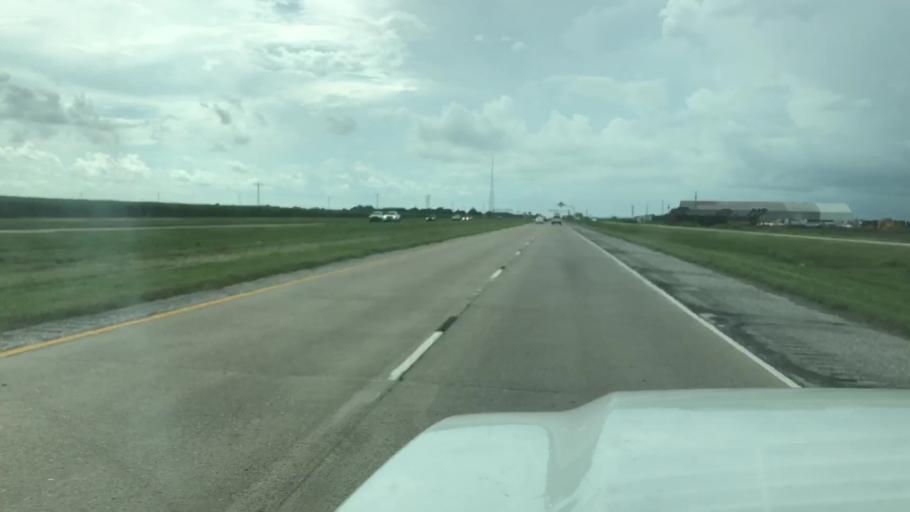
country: US
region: Louisiana
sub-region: Iberia Parish
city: Jeanerette
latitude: 29.9097
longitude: -91.7133
